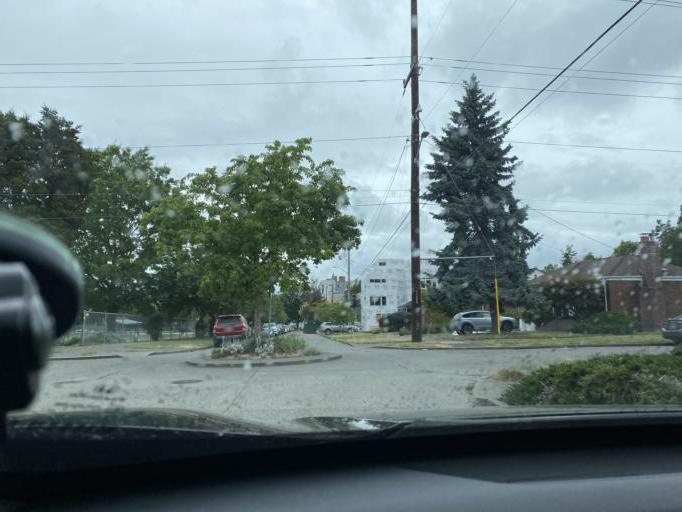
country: US
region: Washington
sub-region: King County
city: Seattle
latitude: 47.6679
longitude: -122.3683
